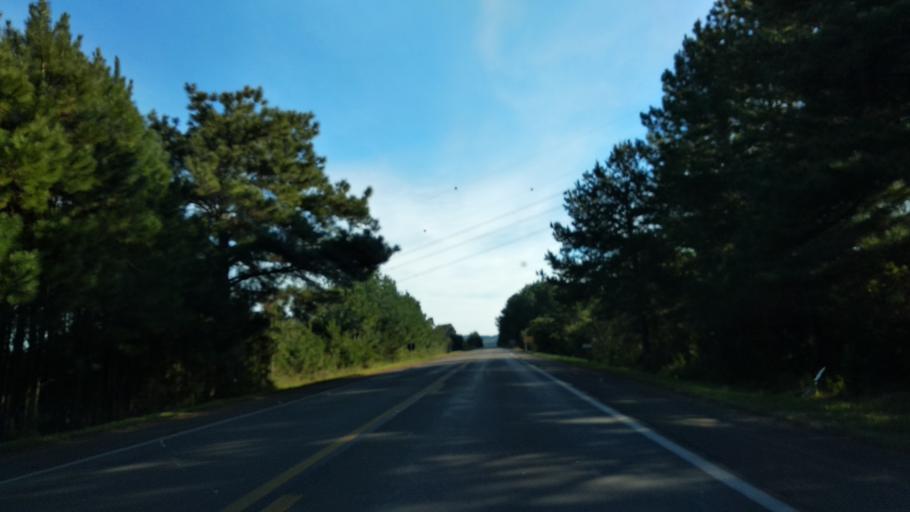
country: BR
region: Santa Catarina
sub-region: Celso Ramos
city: Celso Ramos
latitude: -27.5424
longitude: -51.4191
